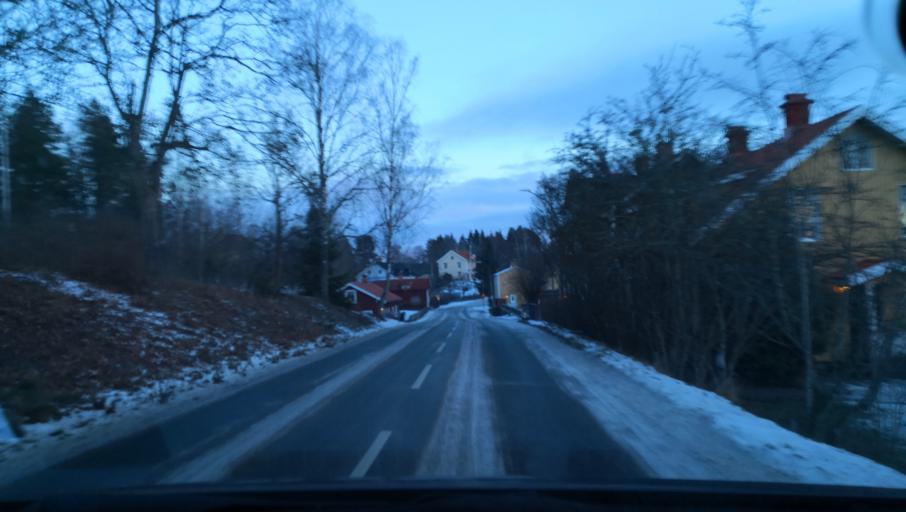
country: SE
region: Soedermanland
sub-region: Katrineholms Kommun
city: Katrineholm
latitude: 59.0894
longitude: 16.2115
